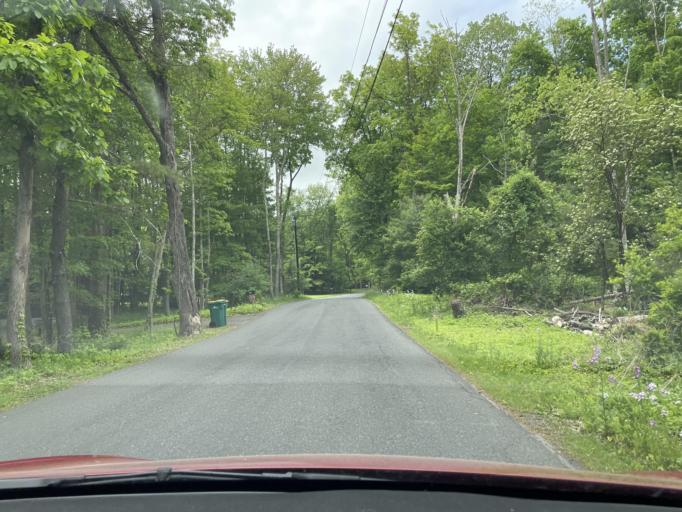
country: US
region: New York
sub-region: Ulster County
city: West Hurley
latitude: 42.0148
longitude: -74.0988
